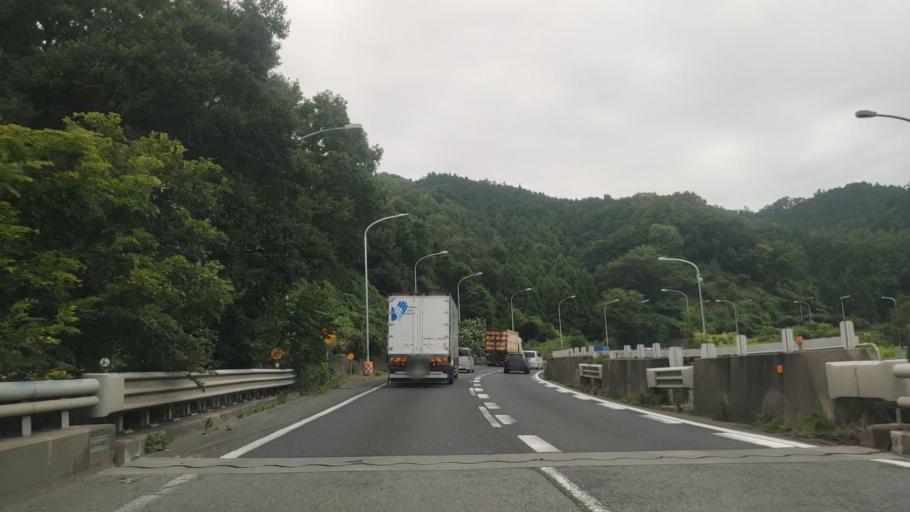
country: JP
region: Nara
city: Tenri
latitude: 34.6176
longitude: 135.8726
